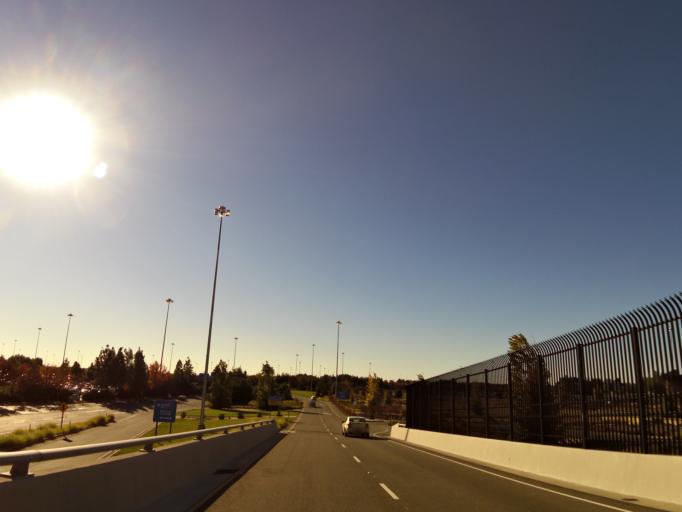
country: US
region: California
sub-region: Yolo County
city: West Sacramento
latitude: 38.6906
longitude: -121.5907
